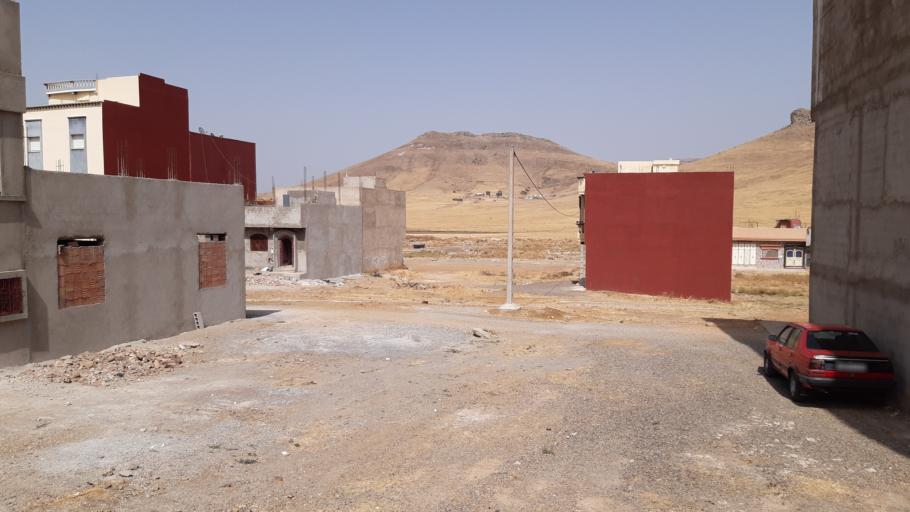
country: MA
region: Meknes-Tafilalet
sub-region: Khenifra
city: Khenifra
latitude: 33.1588
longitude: -5.5662
